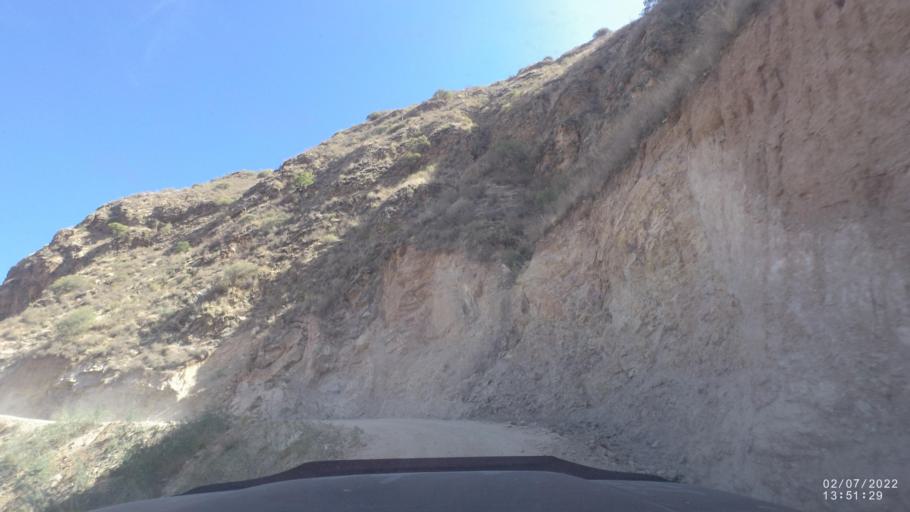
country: BO
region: Cochabamba
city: Irpa Irpa
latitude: -17.8226
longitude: -66.3824
